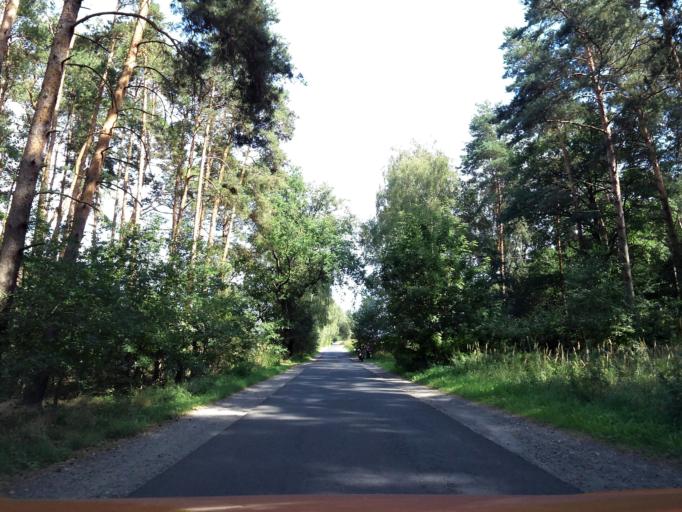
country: DE
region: Brandenburg
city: Michendorf
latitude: 52.2734
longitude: 13.1007
